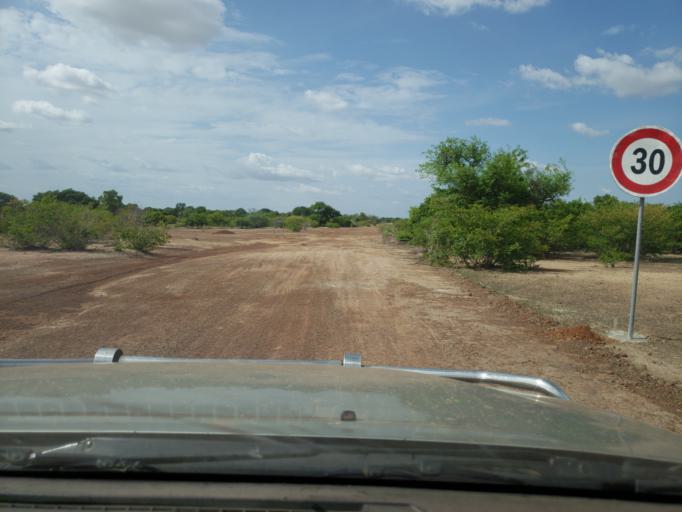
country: ML
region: Segou
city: Bla
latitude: 12.7839
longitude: -5.6074
